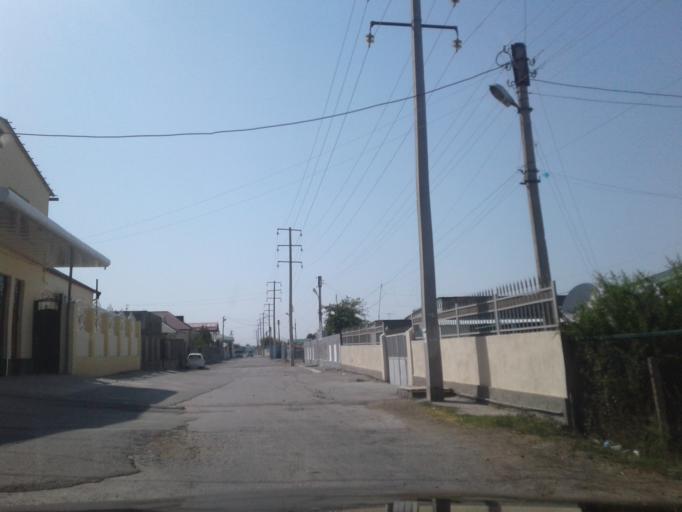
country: TM
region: Ahal
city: Ashgabat
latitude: 37.9726
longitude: 58.4361
